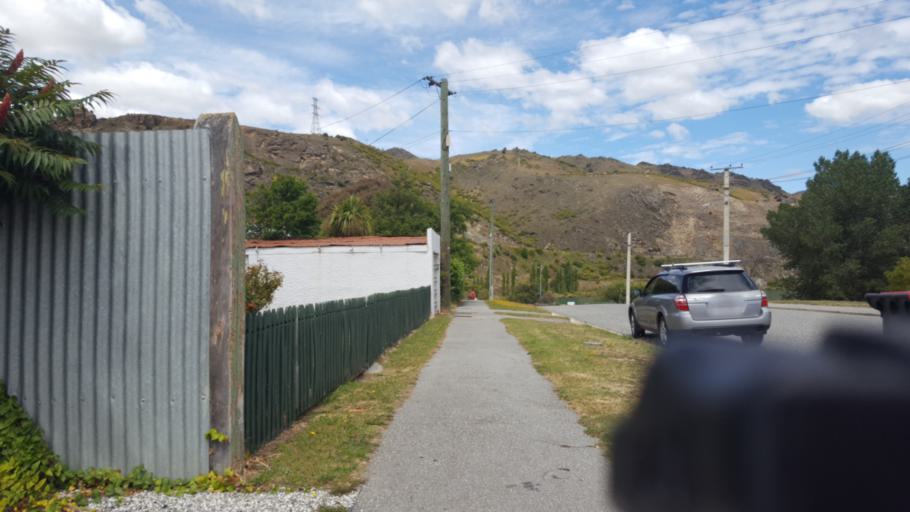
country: NZ
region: Otago
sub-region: Queenstown-Lakes District
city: Wanaka
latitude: -45.0493
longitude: 169.2106
